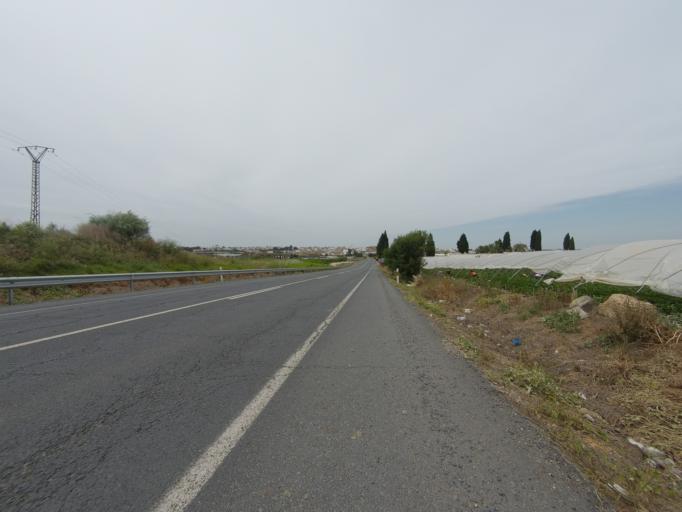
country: ES
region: Andalusia
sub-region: Provincia de Huelva
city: Palos de la Frontera
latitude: 37.2368
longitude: -6.8856
